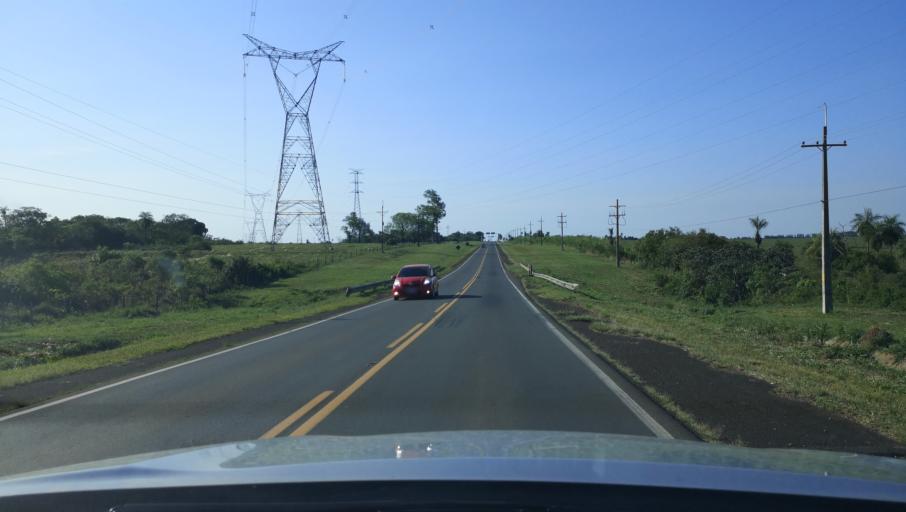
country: PY
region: Misiones
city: Santa Maria
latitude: -26.7899
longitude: -57.0249
